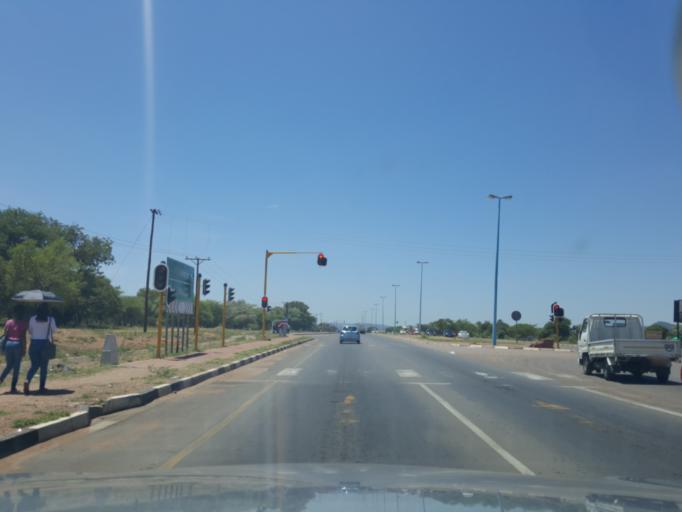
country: BW
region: Kweneng
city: Mogoditshane
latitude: -24.6068
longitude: 25.8578
